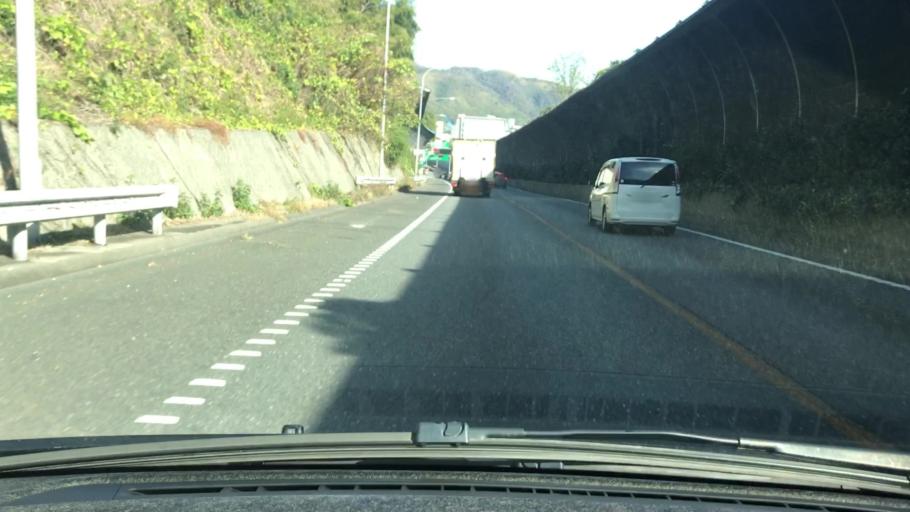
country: JP
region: Kyoto
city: Yawata
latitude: 34.8771
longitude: 135.6555
